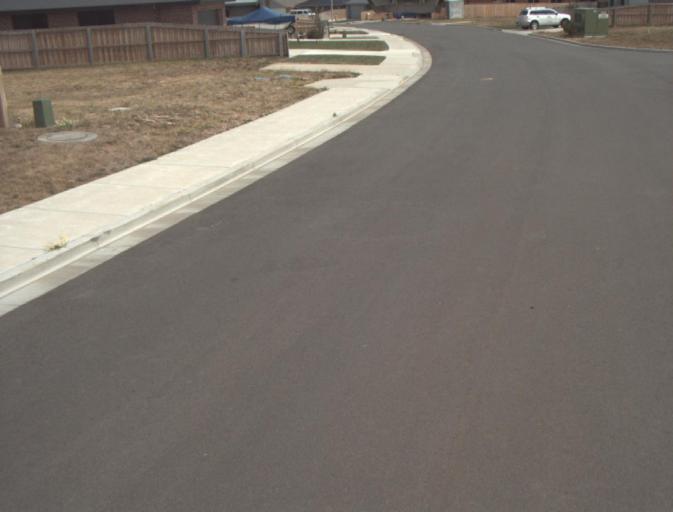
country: AU
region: Tasmania
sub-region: Launceston
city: Mayfield
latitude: -41.3821
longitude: 147.1136
